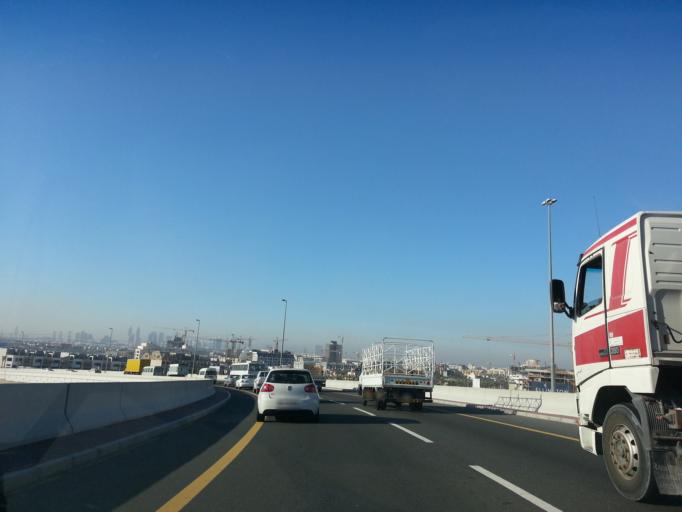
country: AE
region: Dubai
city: Dubai
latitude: 25.0435
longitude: 55.2025
